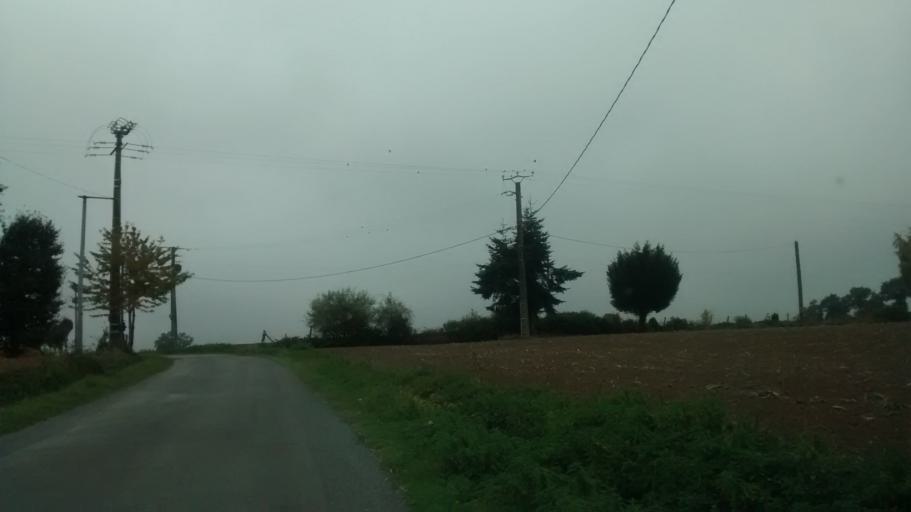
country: FR
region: Brittany
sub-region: Departement d'Ille-et-Vilaine
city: Cintre
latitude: 48.1140
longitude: -1.8978
